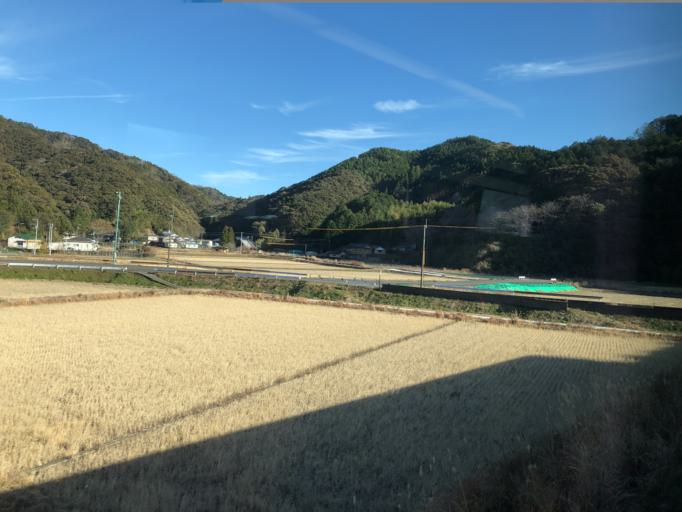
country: JP
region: Kochi
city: Nakamura
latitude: 33.1002
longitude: 133.0995
